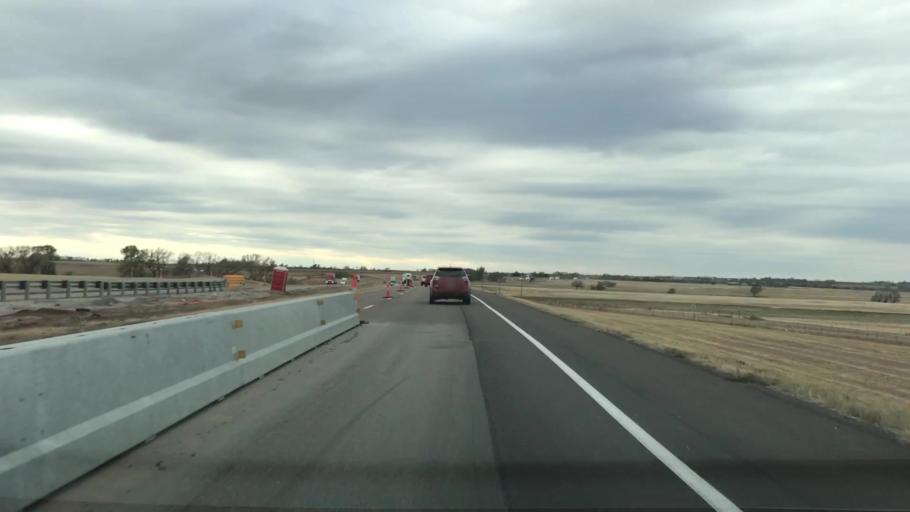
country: US
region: Oklahoma
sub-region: Beckham County
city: Elk City
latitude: 35.4252
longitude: -99.2943
